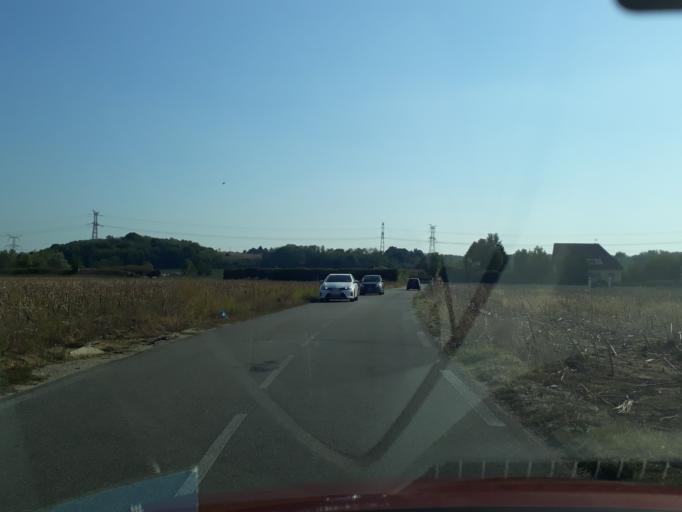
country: FR
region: Rhone-Alpes
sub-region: Departement du Rhone
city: Toussieu
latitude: 45.6730
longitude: 4.9841
